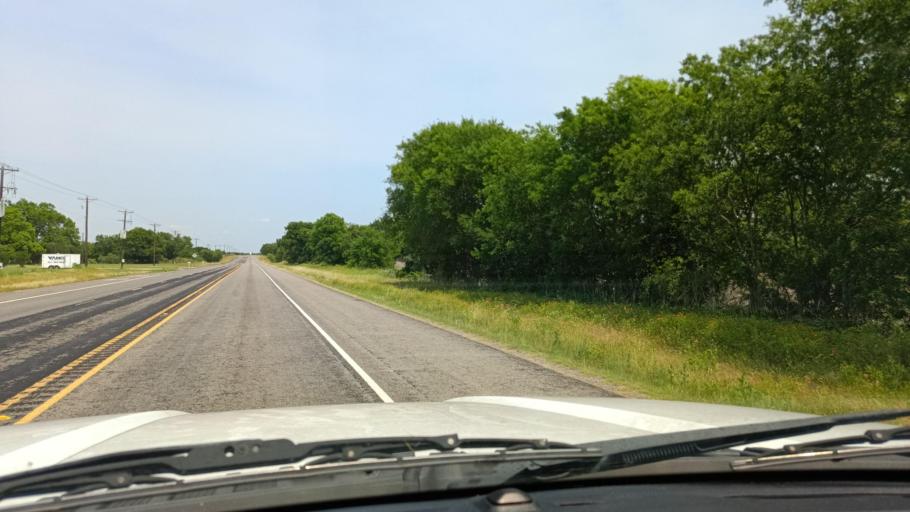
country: US
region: Texas
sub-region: Milam County
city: Cameron
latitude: 30.8488
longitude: -97.0497
